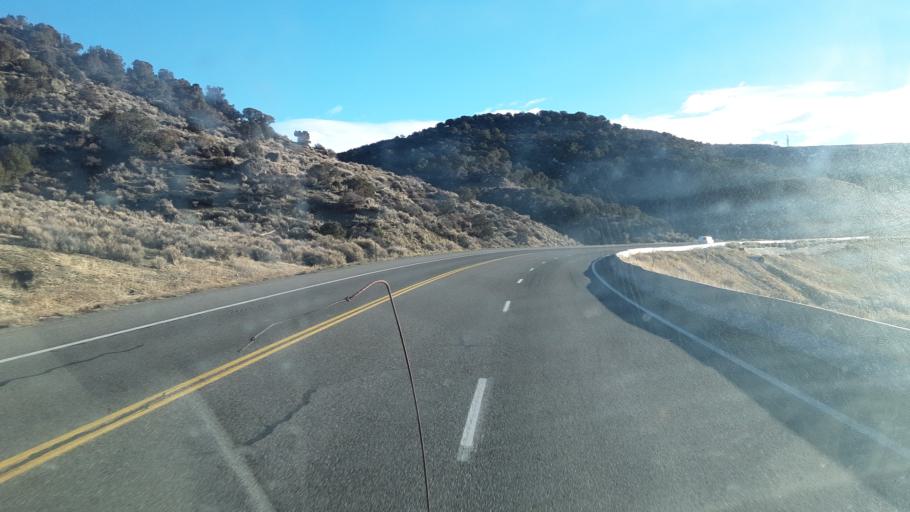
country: US
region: Colorado
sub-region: Montrose County
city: Montrose
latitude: 38.4587
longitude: -107.6717
